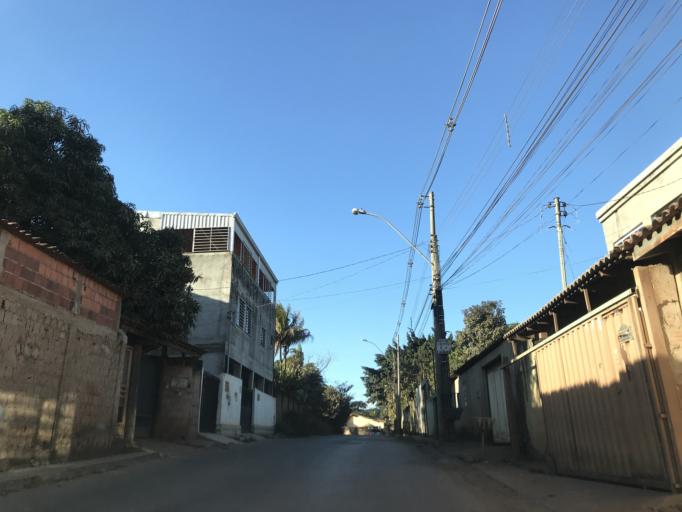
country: BR
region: Federal District
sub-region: Brasilia
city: Brasilia
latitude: -15.8806
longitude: -47.7792
